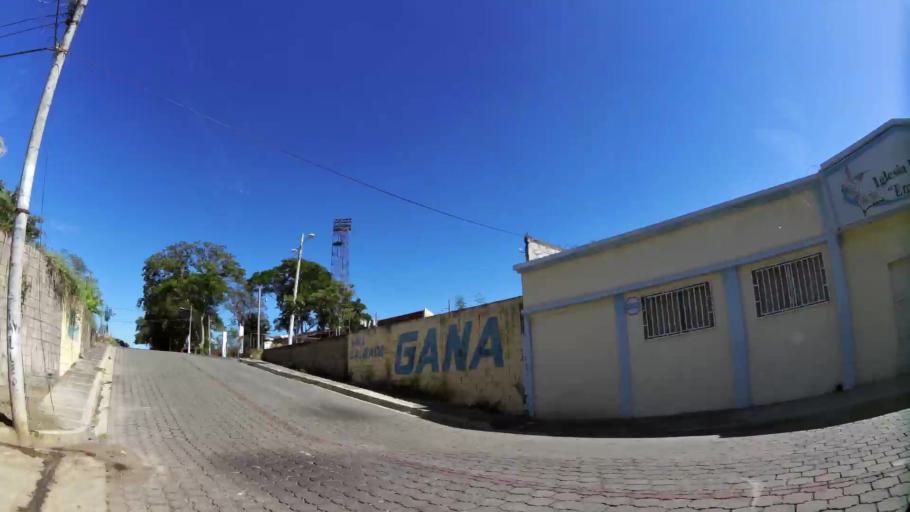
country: SV
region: San Miguel
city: San Miguel
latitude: 13.4816
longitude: -88.1701
